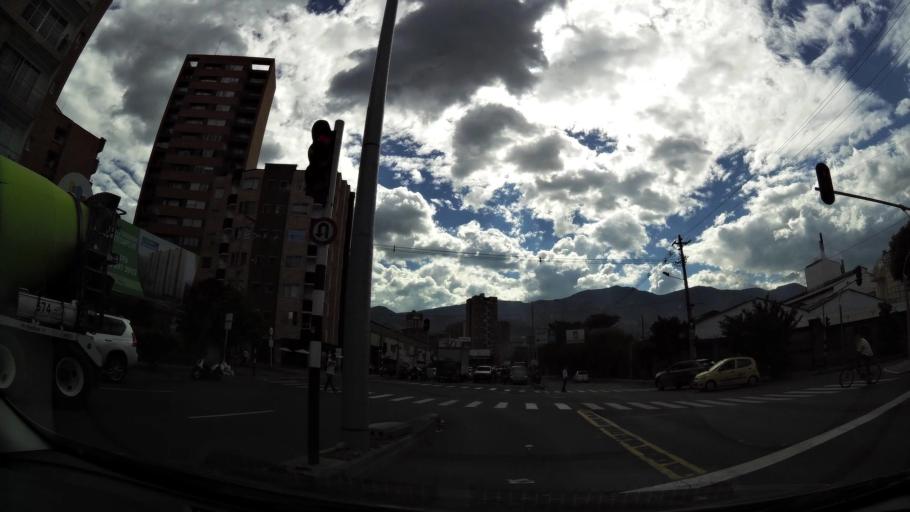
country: CO
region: Antioquia
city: Sabaneta
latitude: 6.1543
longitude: -75.6168
